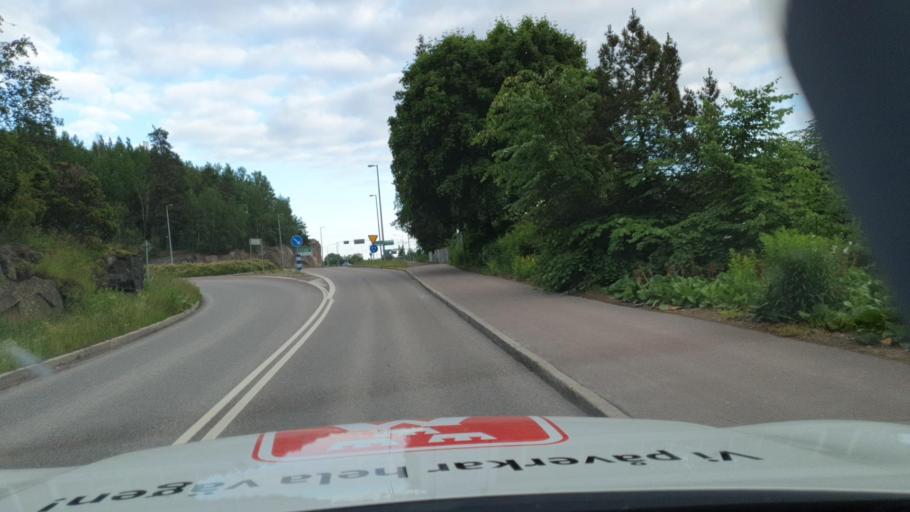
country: SE
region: Vaermland
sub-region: Karlstads Kommun
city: Karlstad
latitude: 59.3986
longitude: 13.5150
